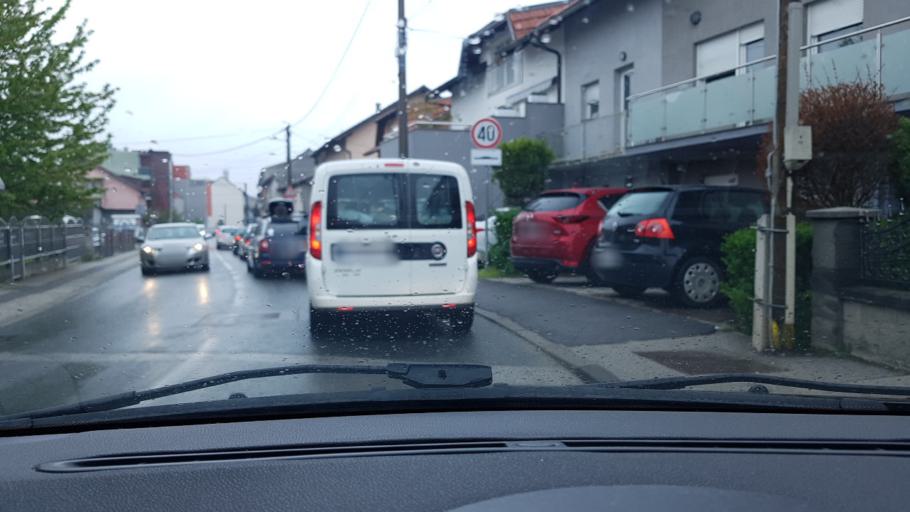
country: HR
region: Grad Zagreb
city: Dubrava
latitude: 45.8110
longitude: 16.0527
